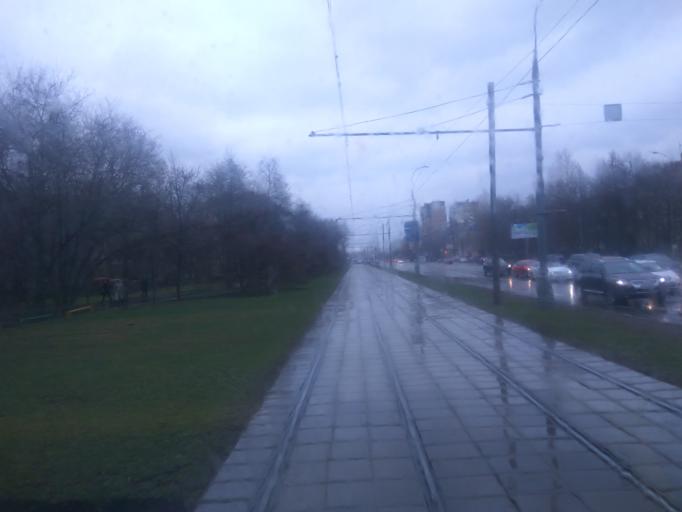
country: RU
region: Moscow
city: Leonovo
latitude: 55.8654
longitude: 37.6620
